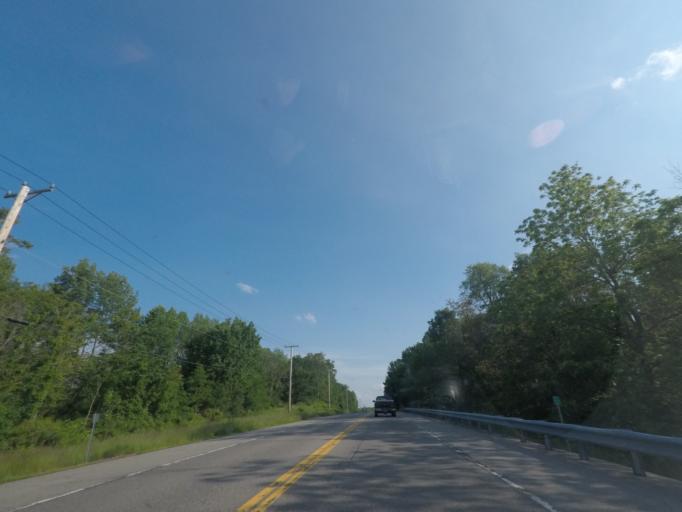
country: US
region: New York
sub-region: Orange County
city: Beaverdam Lake-Salisbury Mills
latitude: 41.4920
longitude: -74.1319
